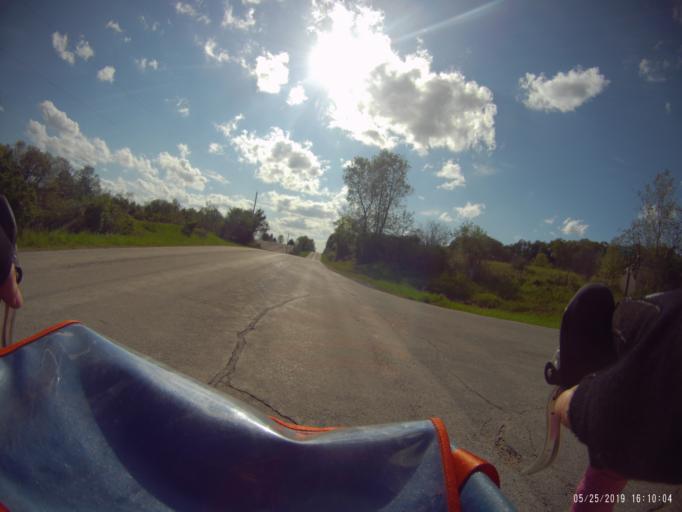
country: US
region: Wisconsin
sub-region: Dane County
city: Mount Horeb
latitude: 42.9629
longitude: -89.6624
